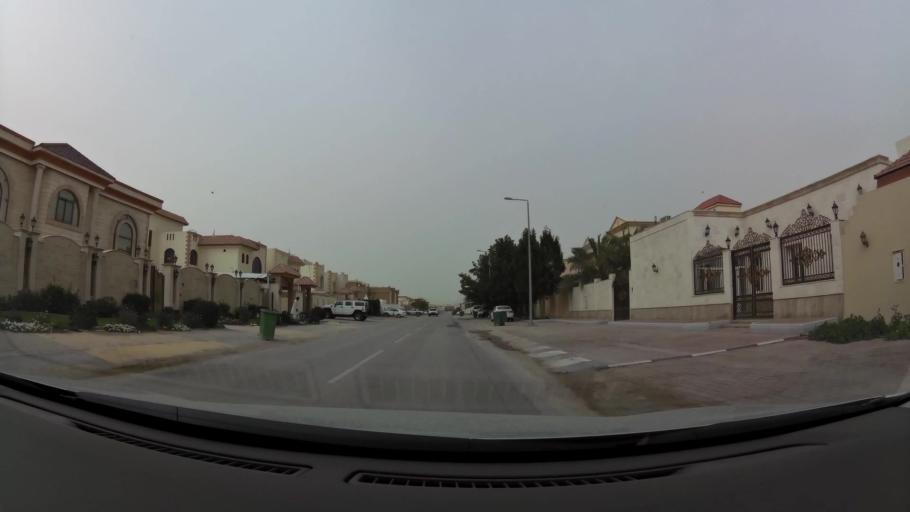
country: QA
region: Baladiyat ad Dawhah
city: Doha
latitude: 25.2405
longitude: 51.5045
